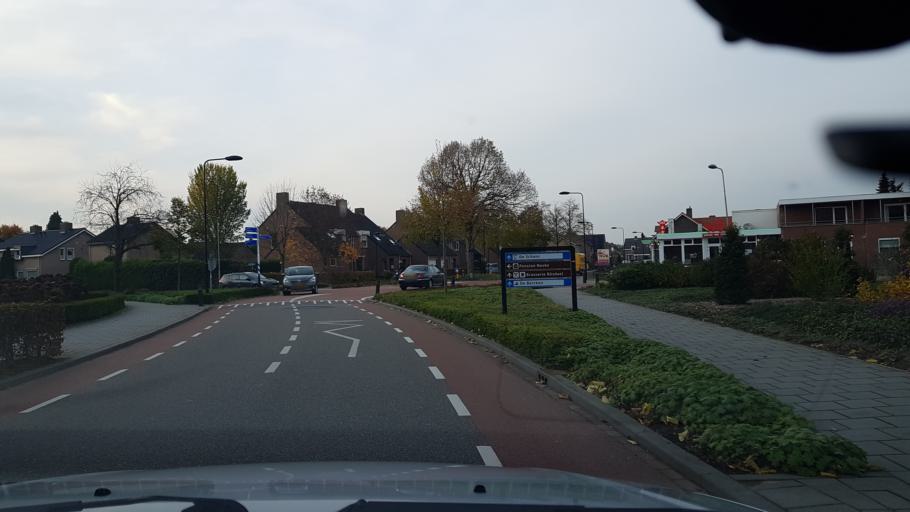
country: NL
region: Limburg
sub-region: Gemeente Beesel
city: Reuver
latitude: 51.2799
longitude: 6.0705
